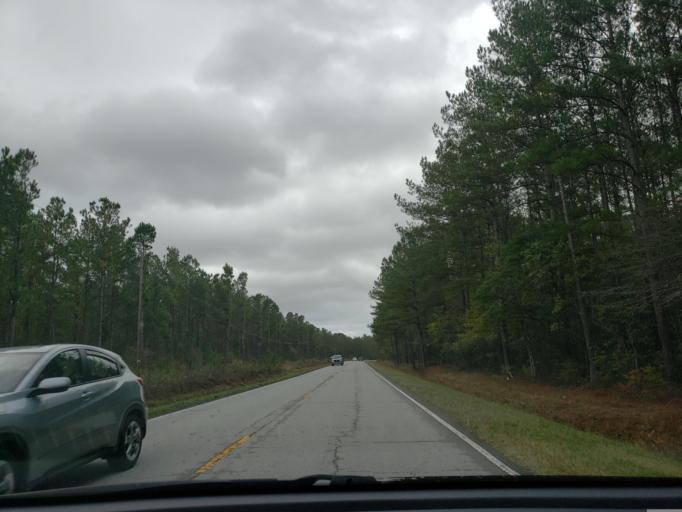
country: US
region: North Carolina
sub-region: Onslow County
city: Half Moon
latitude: 34.7310
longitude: -77.5945
